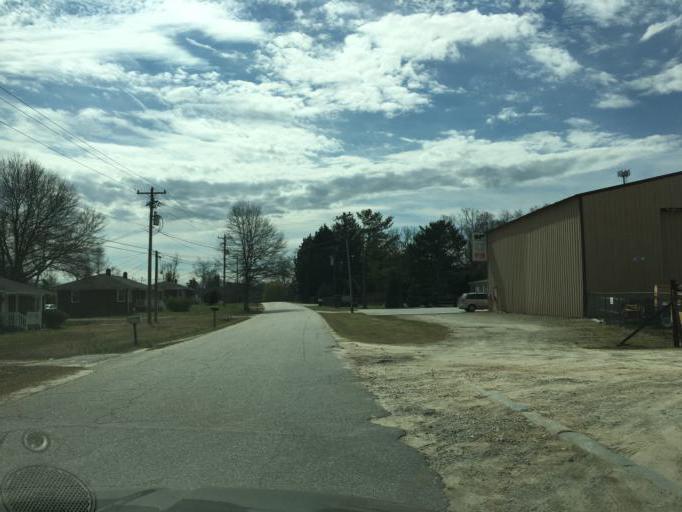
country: US
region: South Carolina
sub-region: Greenville County
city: Fountain Inn
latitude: 34.7037
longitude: -82.2269
